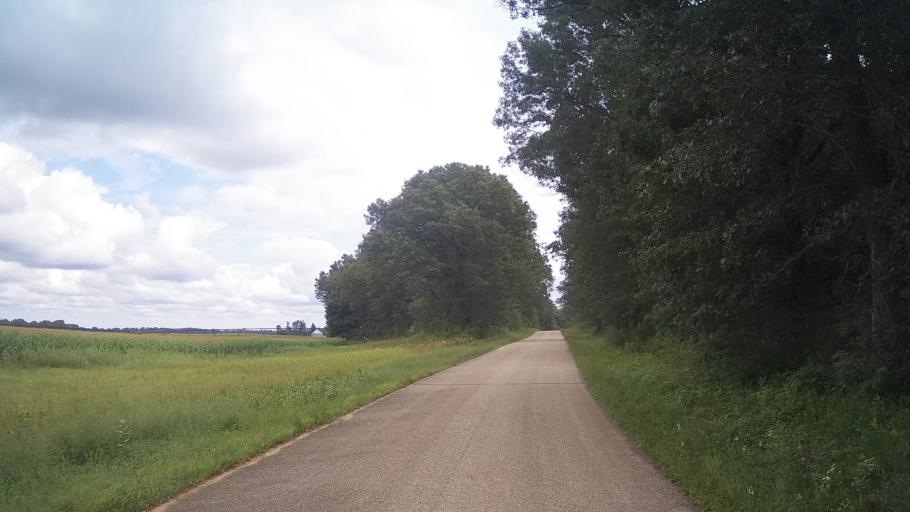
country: US
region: Wisconsin
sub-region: Adams County
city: Friendship
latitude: 44.0293
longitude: -89.9063
